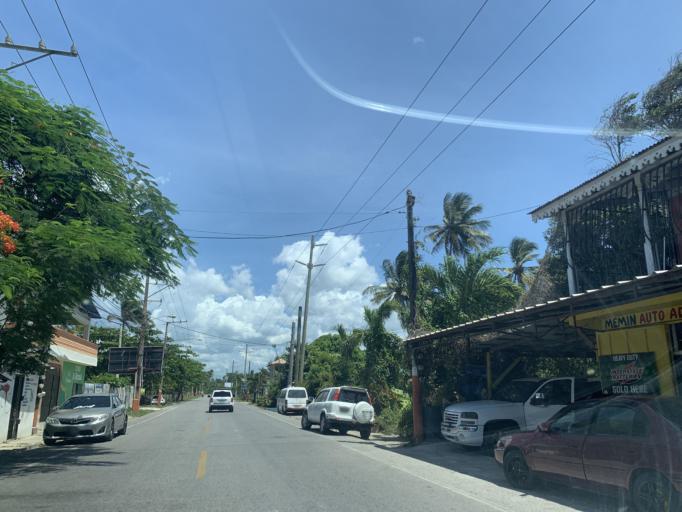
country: DO
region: Puerto Plata
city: Cabarete
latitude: 19.7395
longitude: -70.3916
